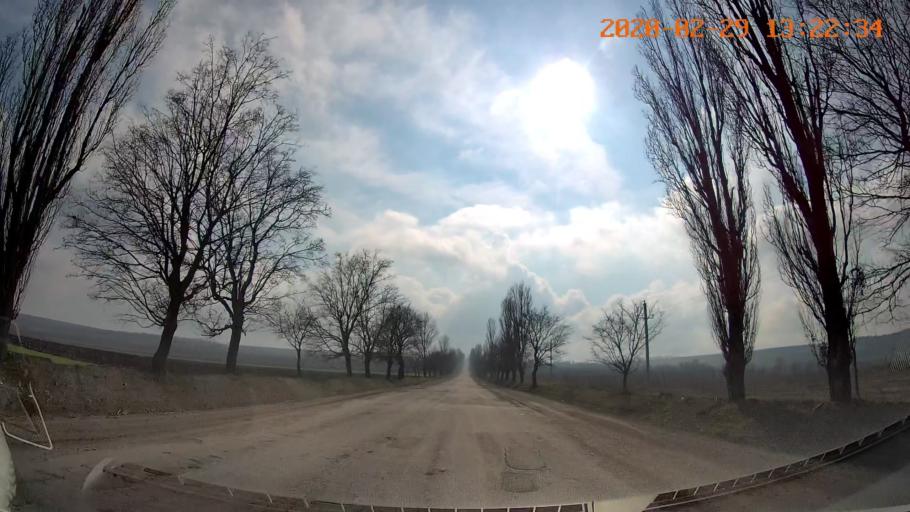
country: MD
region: Telenesti
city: Camenca
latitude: 47.9590
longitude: 28.6276
